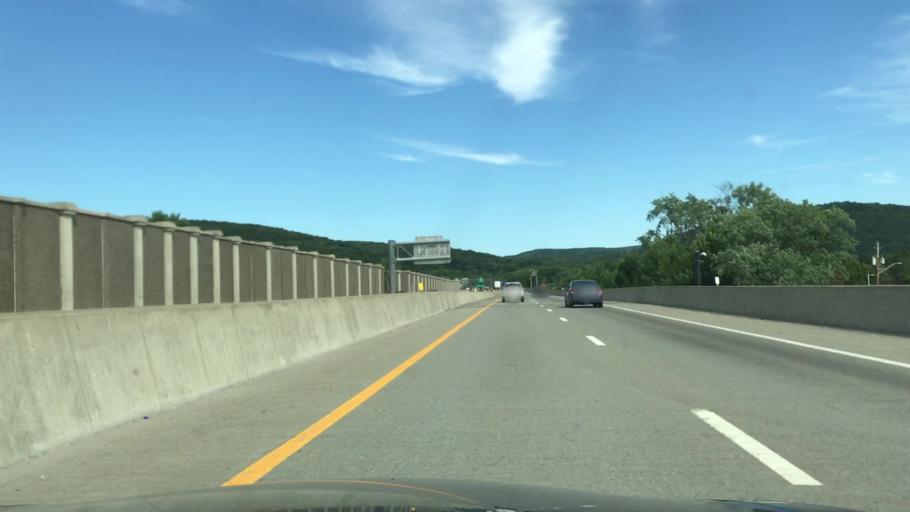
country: US
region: New York
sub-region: Chemung County
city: Horseheads
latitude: 42.1574
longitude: -76.8218
